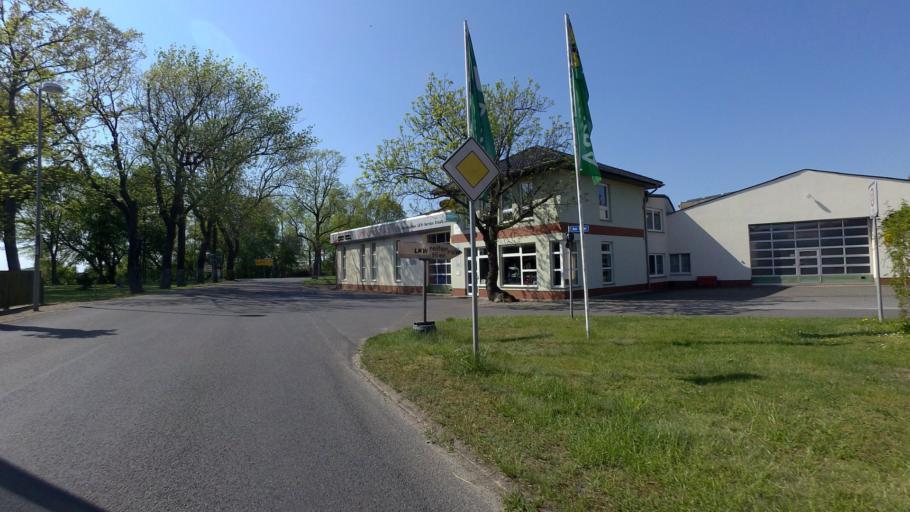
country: DE
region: Brandenburg
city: Schlepzig
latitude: 52.0815
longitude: 13.8737
